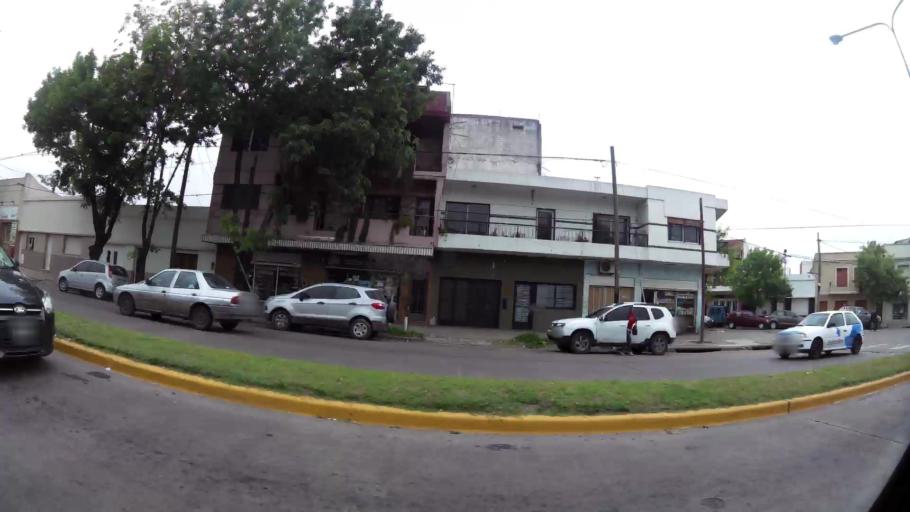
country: AR
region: Buenos Aires
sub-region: Partido de La Plata
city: La Plata
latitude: -34.9223
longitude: -57.9780
